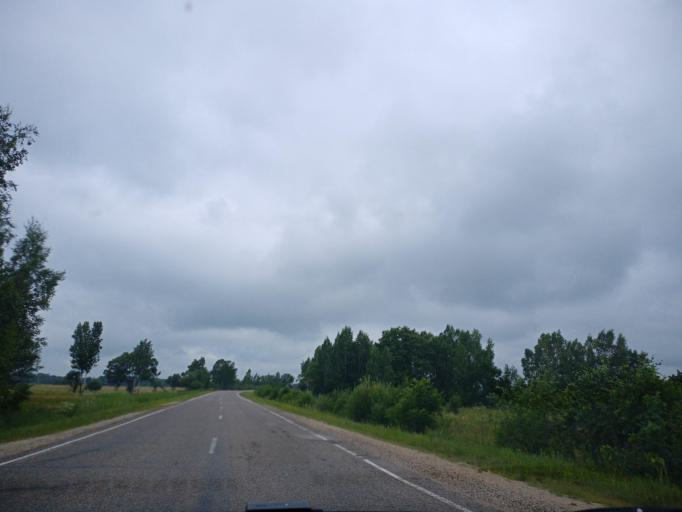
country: RU
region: Primorskiy
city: Novopokrovka
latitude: 45.9643
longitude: 134.2575
